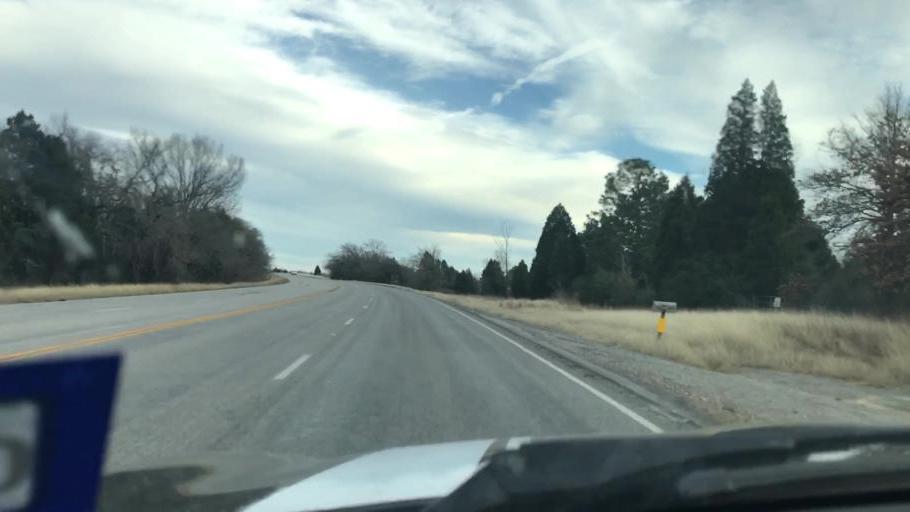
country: US
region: Texas
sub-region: Bastrop County
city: Elgin
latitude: 30.2982
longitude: -97.2863
